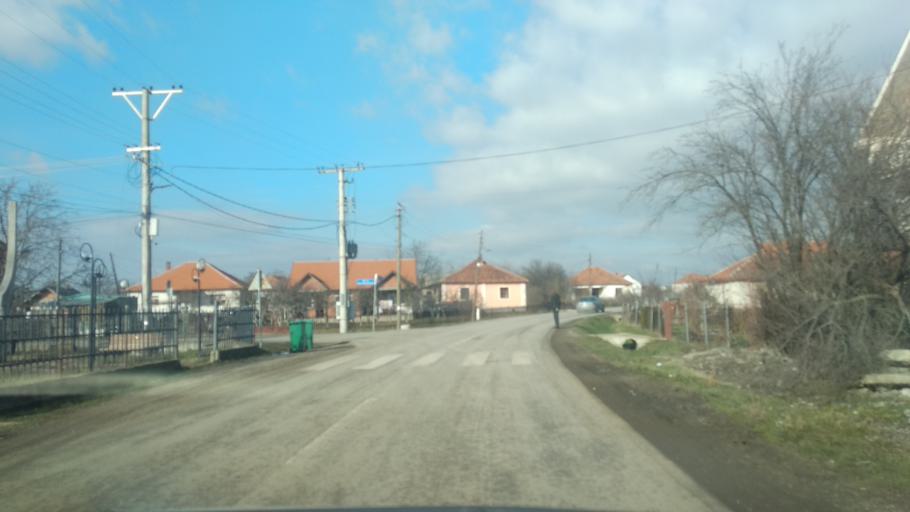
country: XK
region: Pristina
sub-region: Lipjan
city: Lipljan
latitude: 42.5649
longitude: 21.1646
